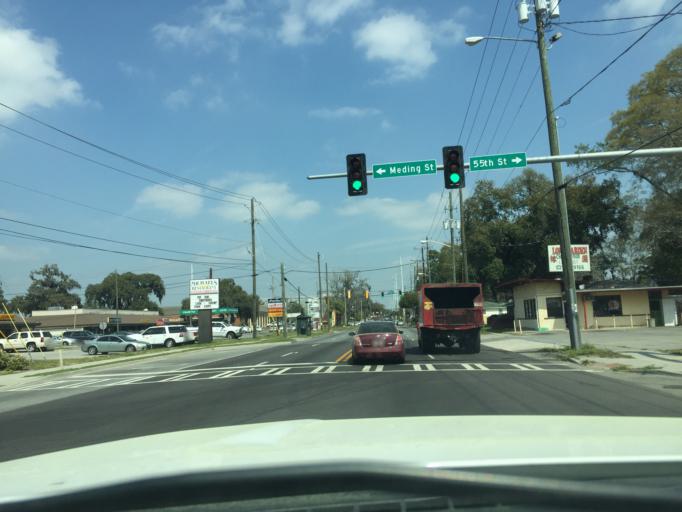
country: US
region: Georgia
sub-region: Chatham County
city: Savannah
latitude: 32.0446
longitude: -81.1095
